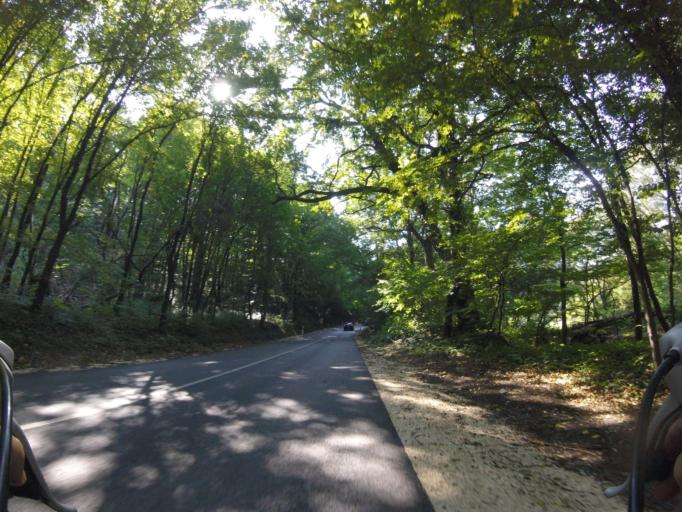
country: HU
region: Komarom-Esztergom
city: Nyergesujfalu
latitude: 47.7085
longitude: 18.5582
